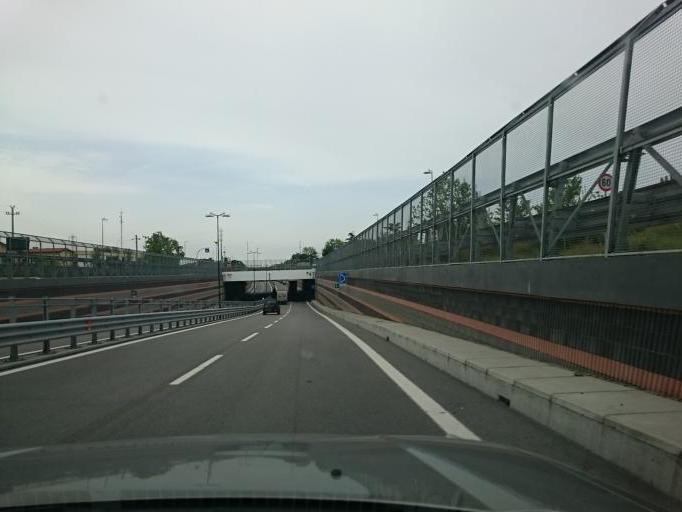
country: IT
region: Veneto
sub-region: Provincia di Venezia
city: Campalto
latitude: 45.4983
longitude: 12.2743
